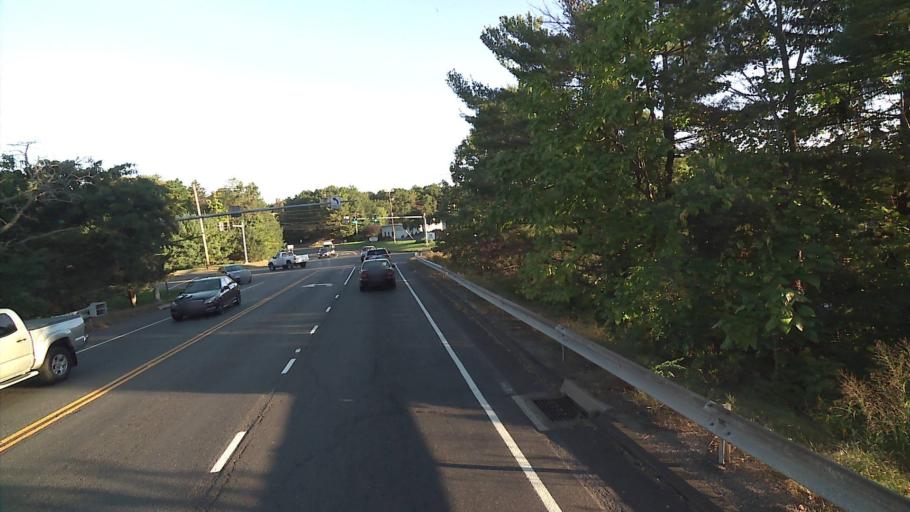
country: US
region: Connecticut
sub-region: New Haven County
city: Wallingford
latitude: 41.4877
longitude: -72.8111
